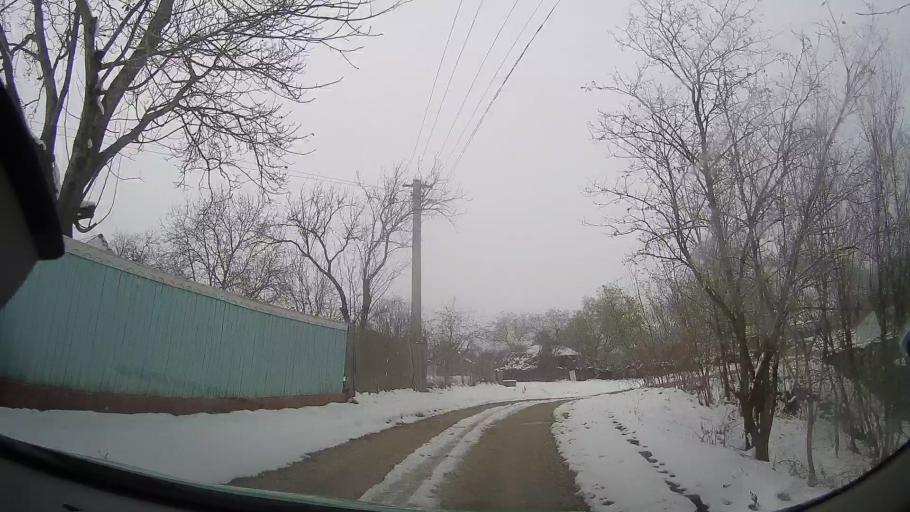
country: RO
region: Bacau
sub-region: Comuna Vultureni
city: Vultureni
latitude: 46.3788
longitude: 27.2853
